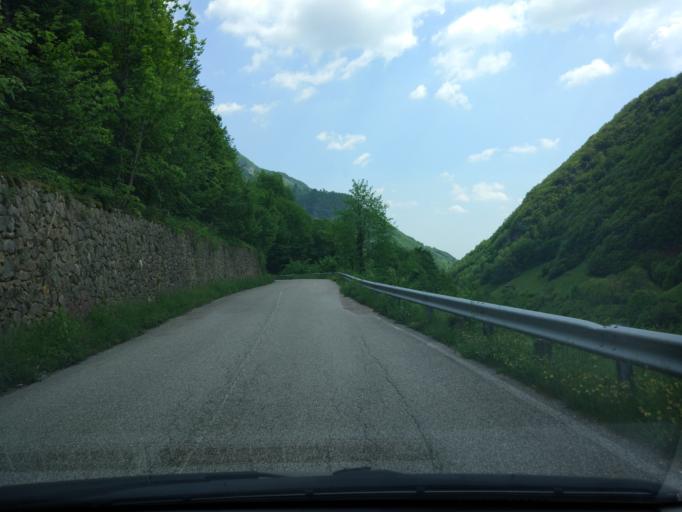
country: IT
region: Veneto
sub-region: Provincia di Verona
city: Selva di Progno
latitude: 45.6587
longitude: 11.1178
